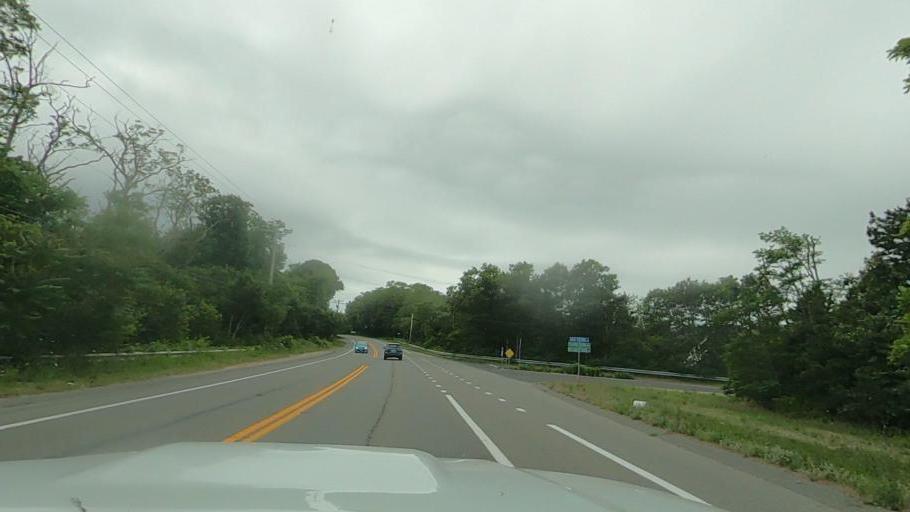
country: US
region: Massachusetts
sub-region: Barnstable County
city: Wellfleet
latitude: 41.9523
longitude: -70.0329
